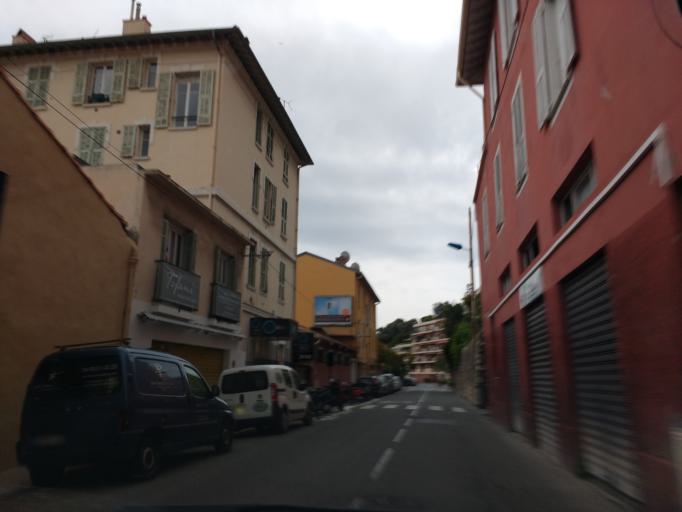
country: FR
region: Provence-Alpes-Cote d'Azur
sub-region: Departement des Alpes-Maritimes
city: Beaulieu-sur-Mer
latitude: 43.7051
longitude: 7.3268
